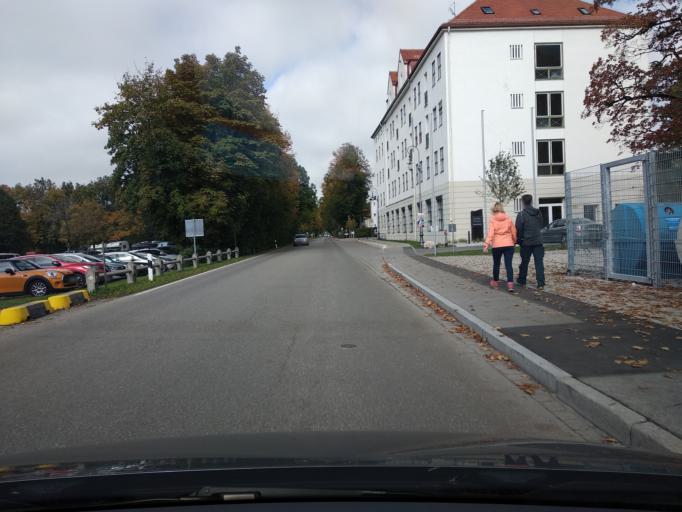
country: DE
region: Bavaria
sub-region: Swabia
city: Schwangau
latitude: 47.5579
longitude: 10.7412
